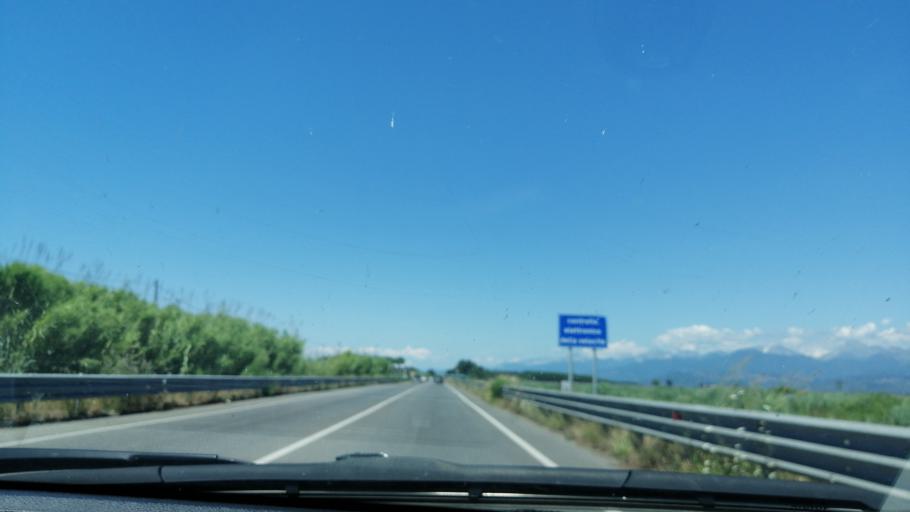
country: IT
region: Tuscany
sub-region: Province of Pisa
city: Migliarino
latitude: 43.7794
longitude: 10.3295
